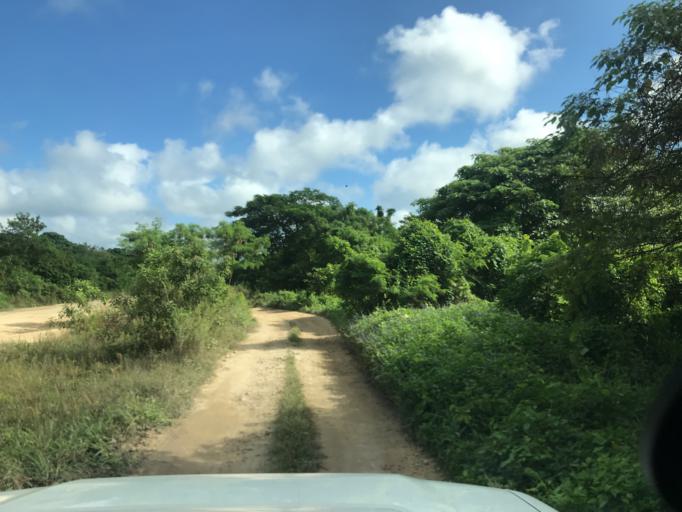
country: VU
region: Sanma
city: Luganville
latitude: -15.5186
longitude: 167.1357
